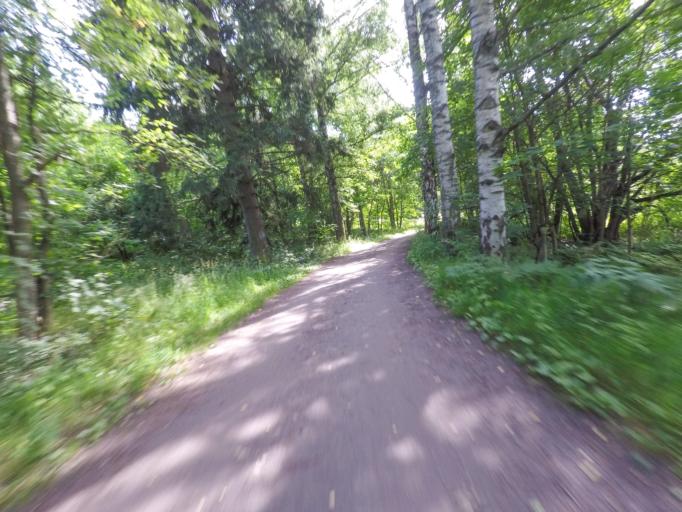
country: FI
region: Uusimaa
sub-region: Helsinki
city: Vantaa
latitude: 60.2010
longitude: 25.0260
